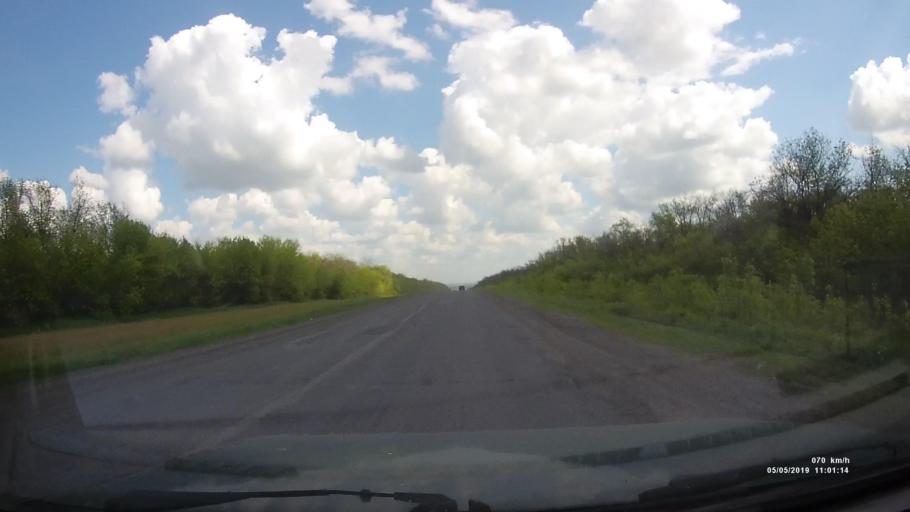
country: RU
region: Rostov
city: Ust'-Donetskiy
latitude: 47.6783
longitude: 40.8970
